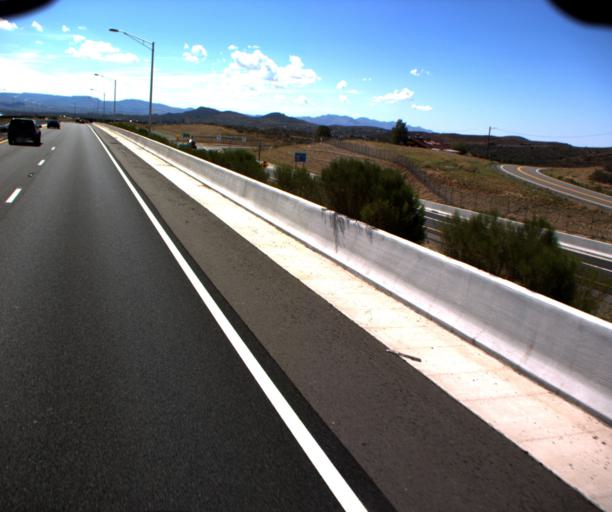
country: US
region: Arizona
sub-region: Yavapai County
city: Spring Valley
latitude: 34.3339
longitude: -112.1276
